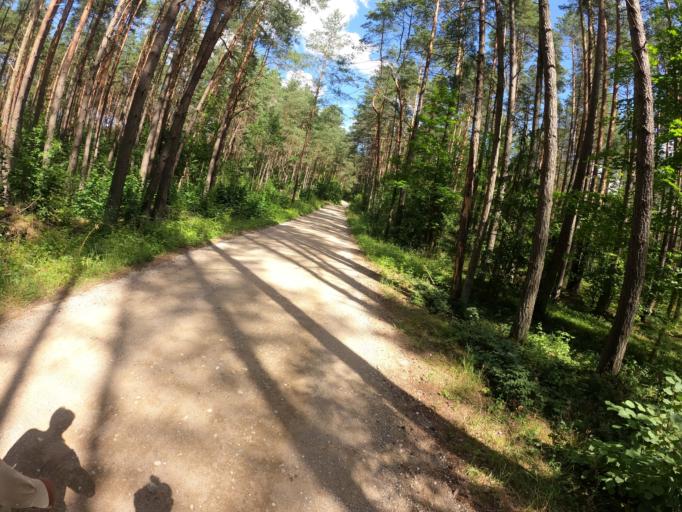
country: LT
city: Birstonas
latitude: 54.6207
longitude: 24.0292
